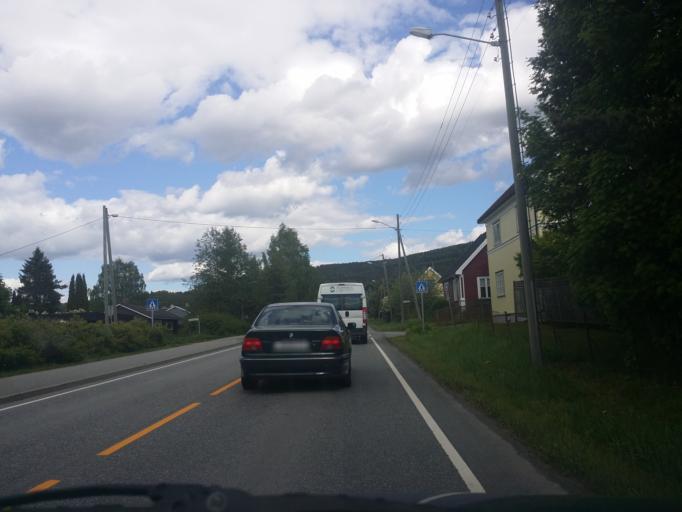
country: NO
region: Oppland
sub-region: Jevnaker
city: Jevnaker
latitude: 60.2419
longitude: 10.4170
